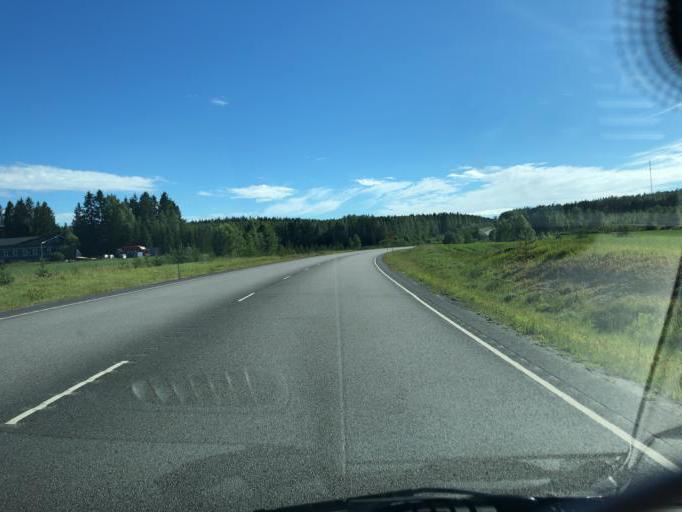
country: FI
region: Uusimaa
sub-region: Loviisa
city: Liljendal
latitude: 60.5989
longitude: 26.1113
